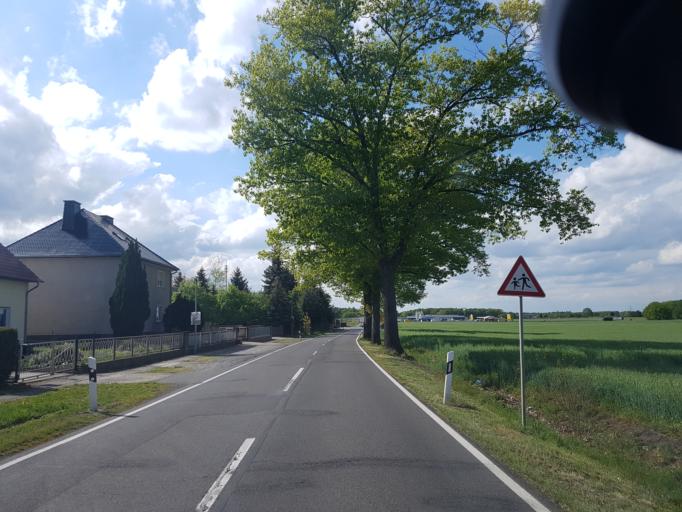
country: DE
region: Brandenburg
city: Drebkau
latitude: 51.6414
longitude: 14.2432
